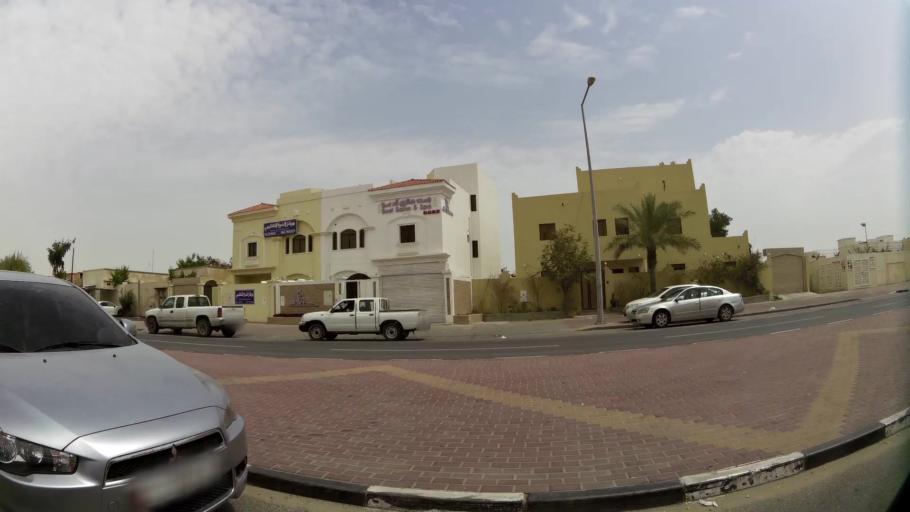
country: QA
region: Baladiyat ad Dawhah
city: Doha
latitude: 25.3176
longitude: 51.4777
